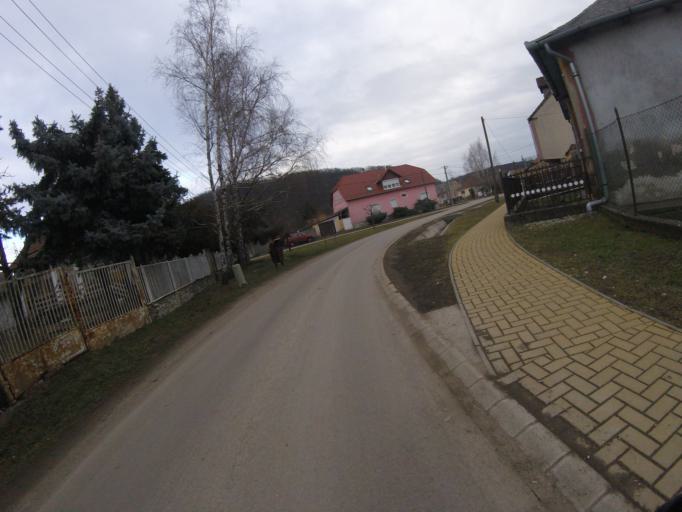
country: HU
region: Heves
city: Egerszalok
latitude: 47.8324
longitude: 20.3321
